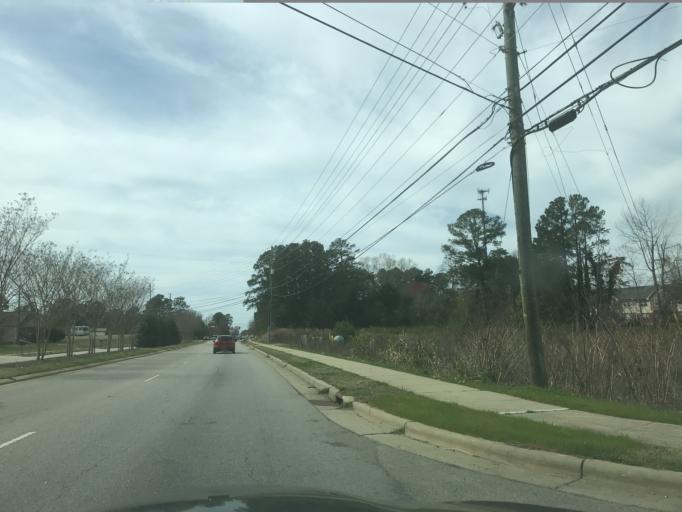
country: US
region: North Carolina
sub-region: Wake County
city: West Raleigh
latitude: 35.7455
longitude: -78.6928
